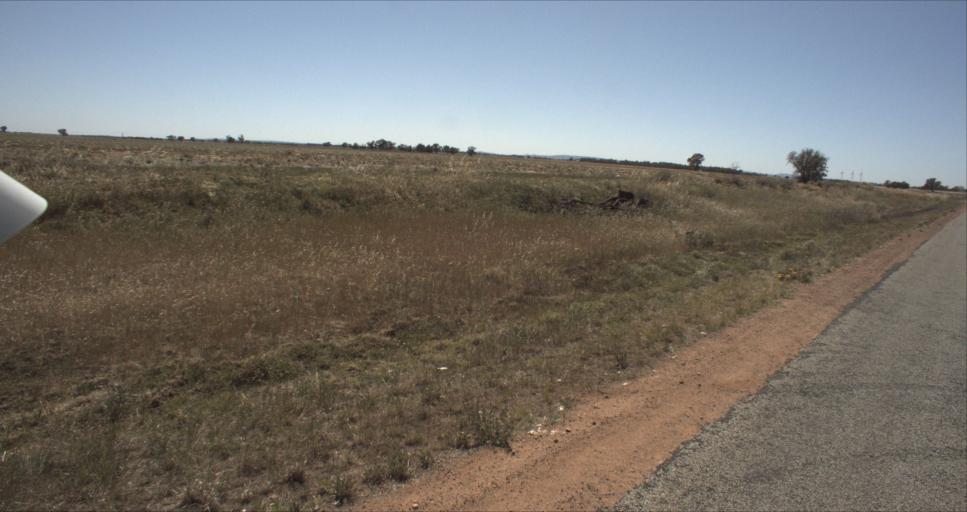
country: AU
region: New South Wales
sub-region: Leeton
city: Leeton
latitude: -34.5807
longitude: 146.2868
